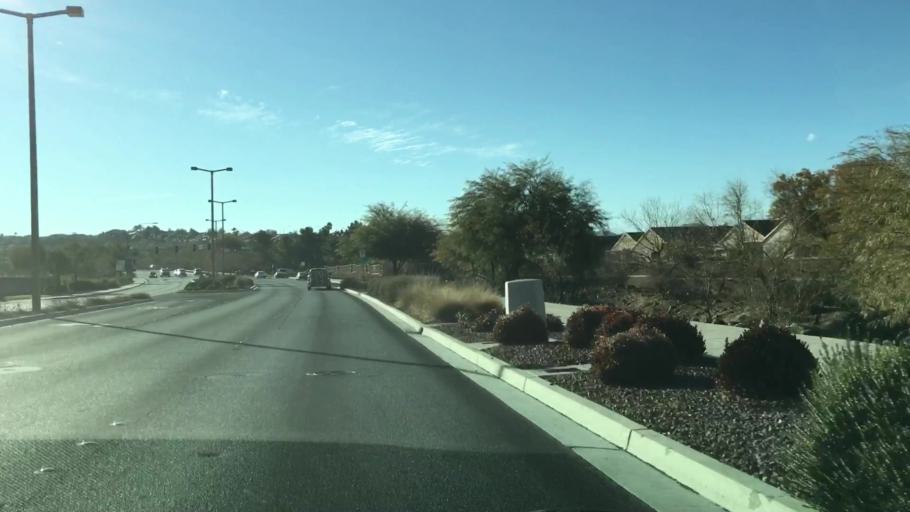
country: US
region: Nevada
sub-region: Clark County
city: Whitney
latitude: 35.9628
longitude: -115.1207
